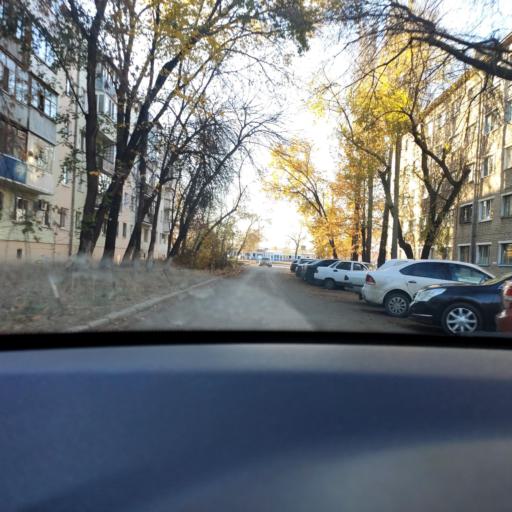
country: RU
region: Samara
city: Samara
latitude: 53.2132
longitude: 50.1979
